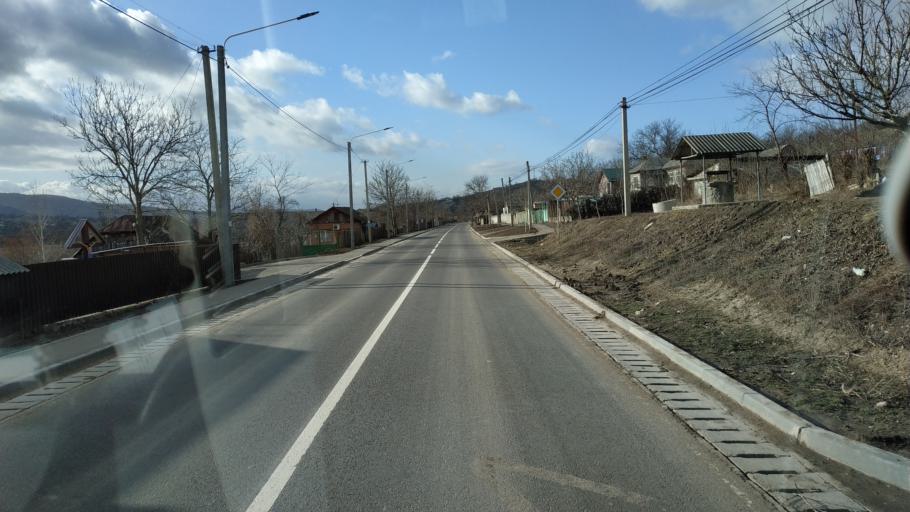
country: MD
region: Calarasi
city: Calarasi
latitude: 47.2853
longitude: 28.1994
